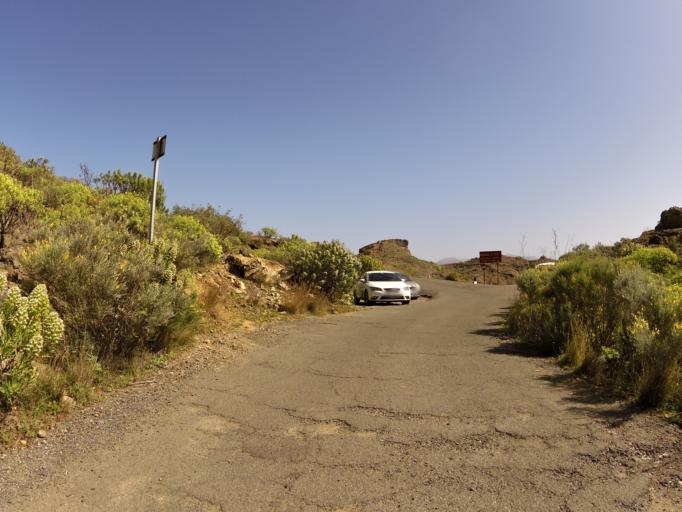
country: ES
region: Canary Islands
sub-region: Provincia de Las Palmas
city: Mogan
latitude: 27.9048
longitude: -15.6865
